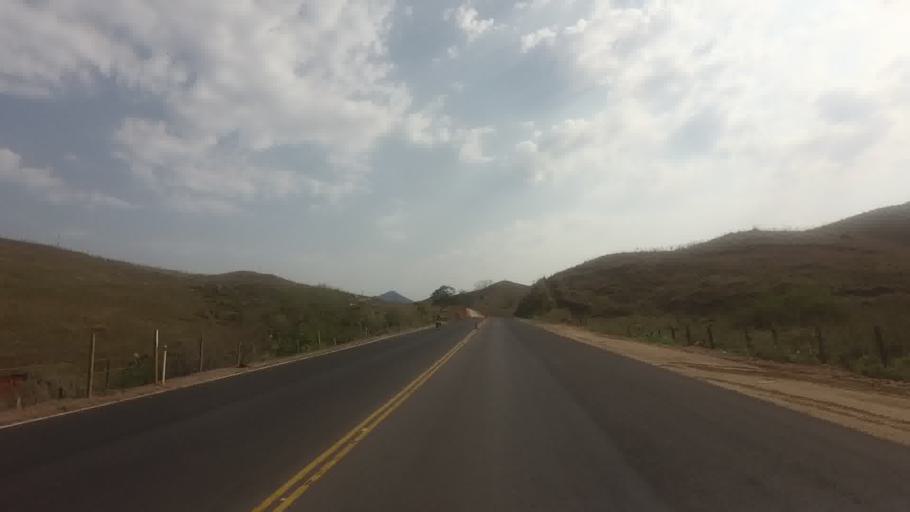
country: BR
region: Rio de Janeiro
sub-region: Itaperuna
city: Itaperuna
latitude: -21.2905
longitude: -41.8035
